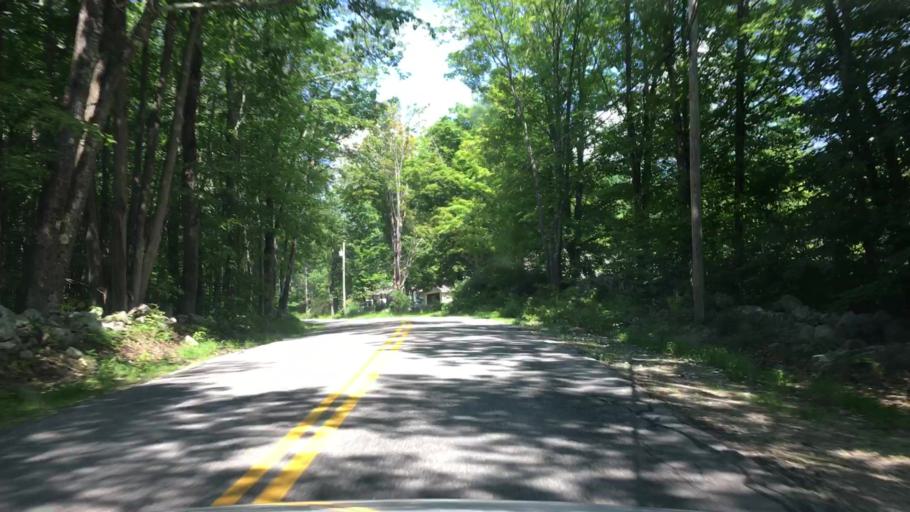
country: US
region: Maine
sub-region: Cumberland County
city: Raymond
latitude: 43.9405
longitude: -70.5230
